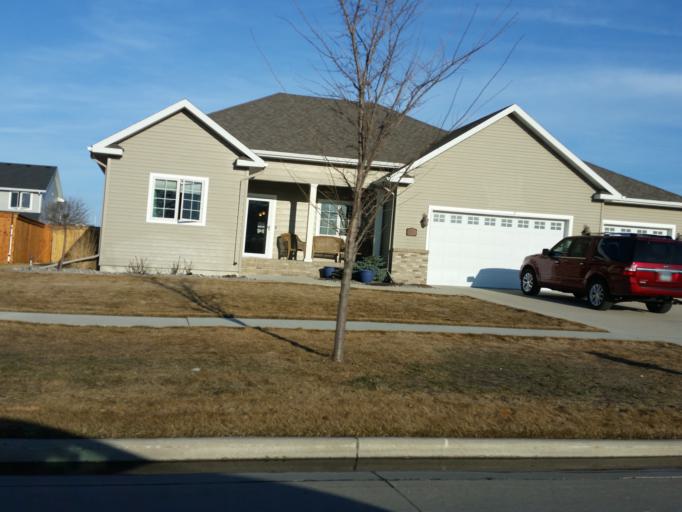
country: US
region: North Dakota
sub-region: Grand Forks County
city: Grand Forks
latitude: 47.8656
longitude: -97.0281
